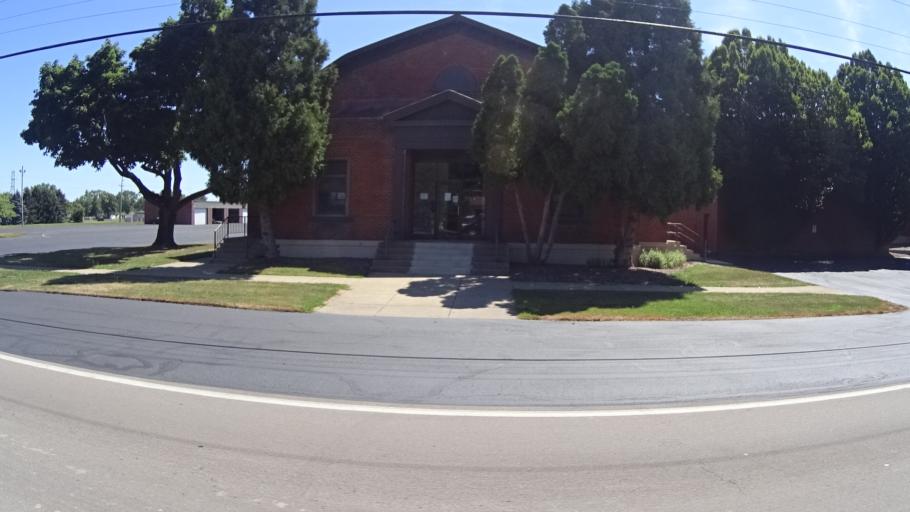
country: US
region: Ohio
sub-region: Erie County
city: Sandusky
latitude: 41.4137
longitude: -82.7030
